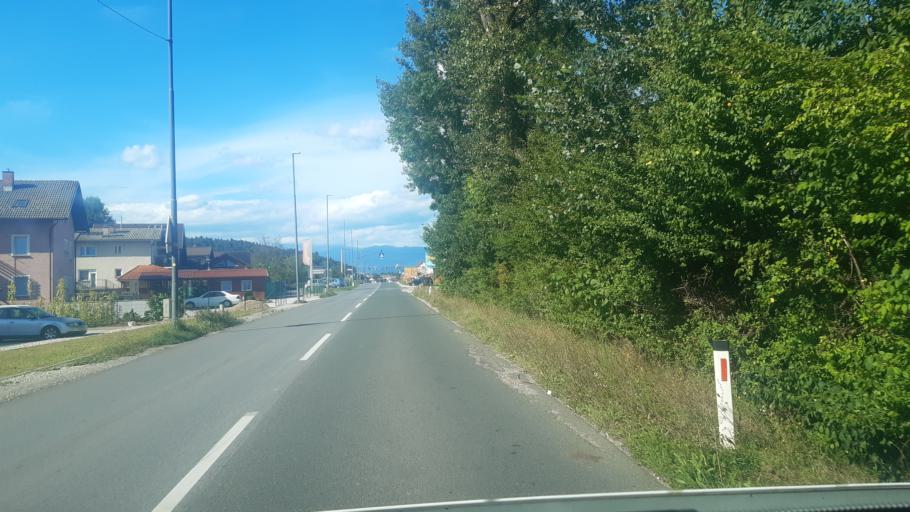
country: SI
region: Dol pri Ljubljani
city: Dol pri Ljubljani
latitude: 46.0889
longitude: 14.5824
